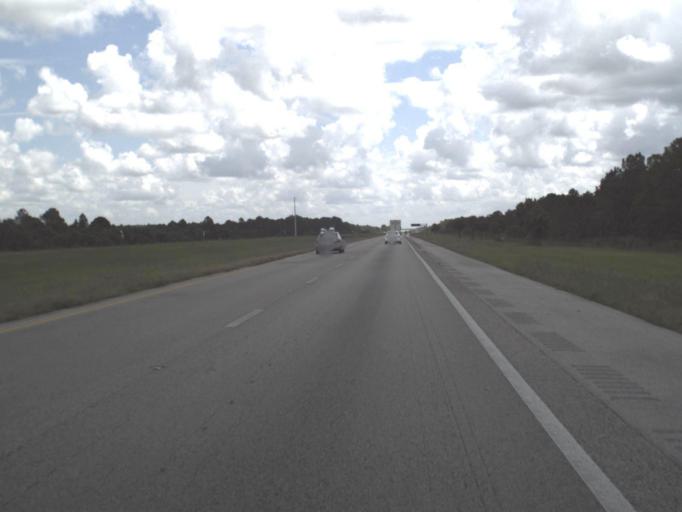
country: US
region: Florida
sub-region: Collier County
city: Golden Gate
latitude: 26.1530
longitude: -81.5683
